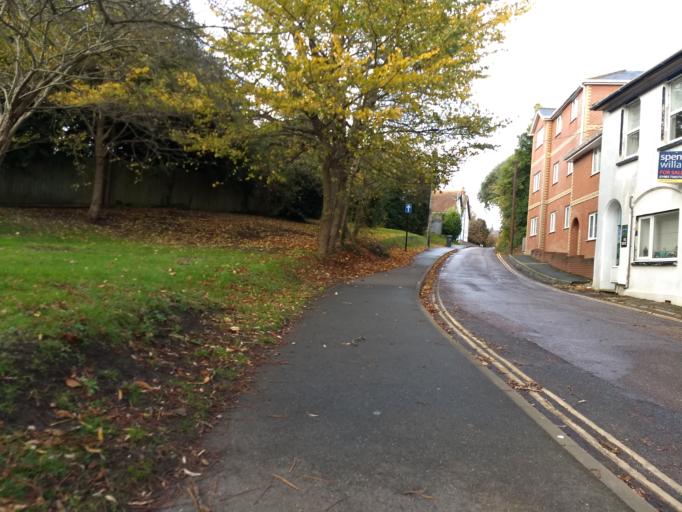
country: GB
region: England
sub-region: Isle of Wight
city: Totland
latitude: 50.6816
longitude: -1.5258
